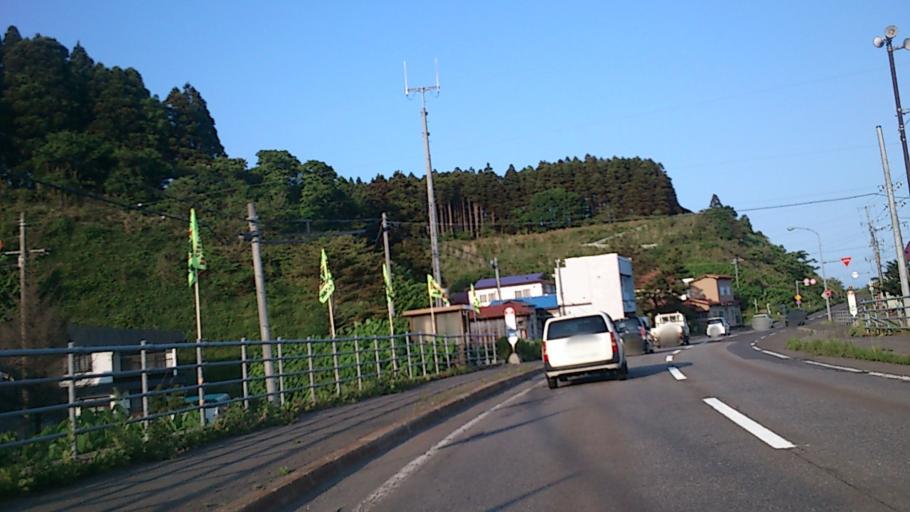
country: JP
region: Hokkaido
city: Kamiiso
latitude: 41.4653
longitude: 140.2485
